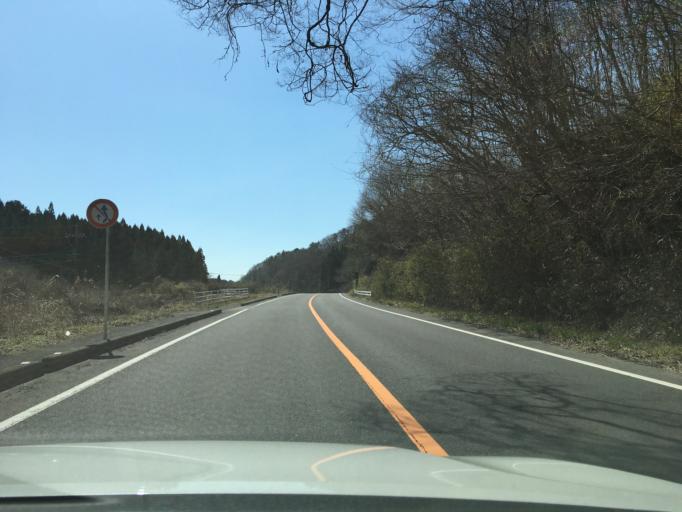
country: JP
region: Tochigi
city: Kuroiso
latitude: 37.0639
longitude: 140.1816
